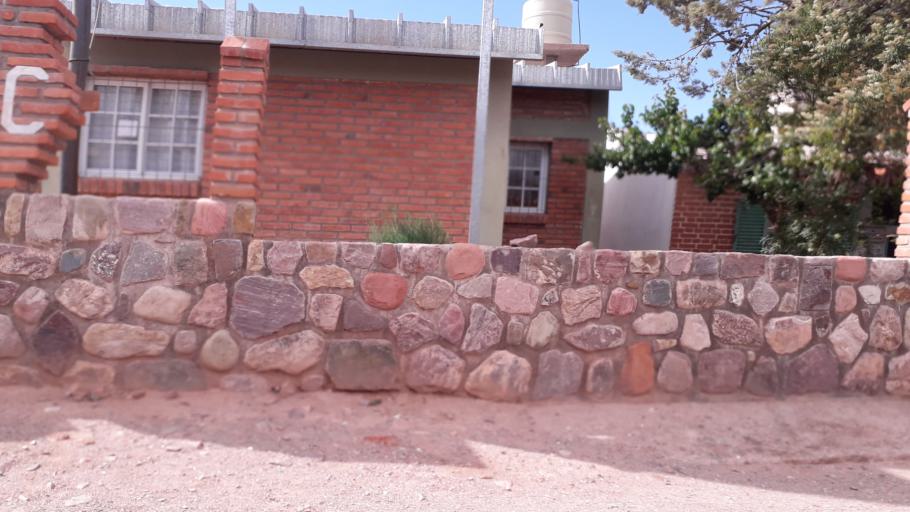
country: AR
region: Jujuy
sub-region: Departamento de Humahuaca
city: Humahuaca
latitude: -23.3044
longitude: -65.3564
